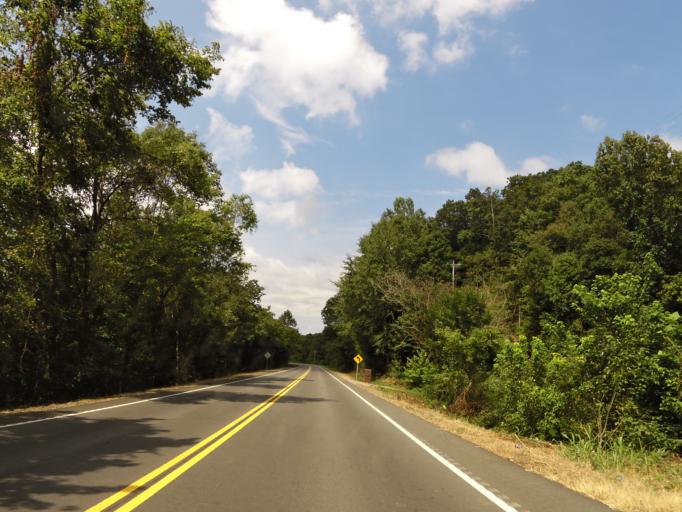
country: US
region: Tennessee
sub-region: Perry County
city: Linden
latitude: 35.7541
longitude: -87.8016
